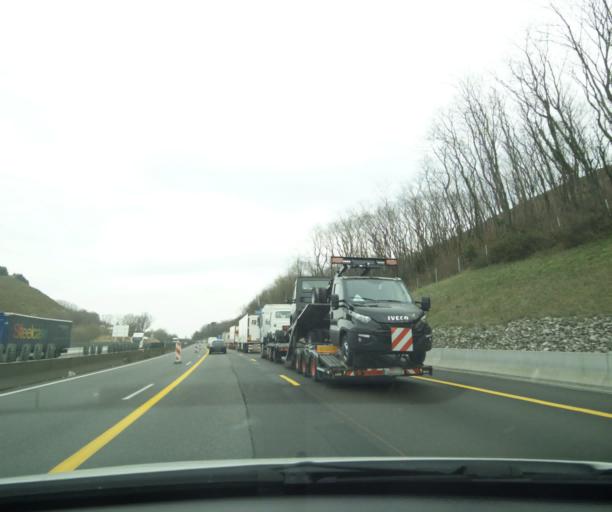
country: FR
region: Aquitaine
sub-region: Departement des Pyrenees-Atlantiques
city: Urrugne
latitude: 43.3408
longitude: -1.7380
